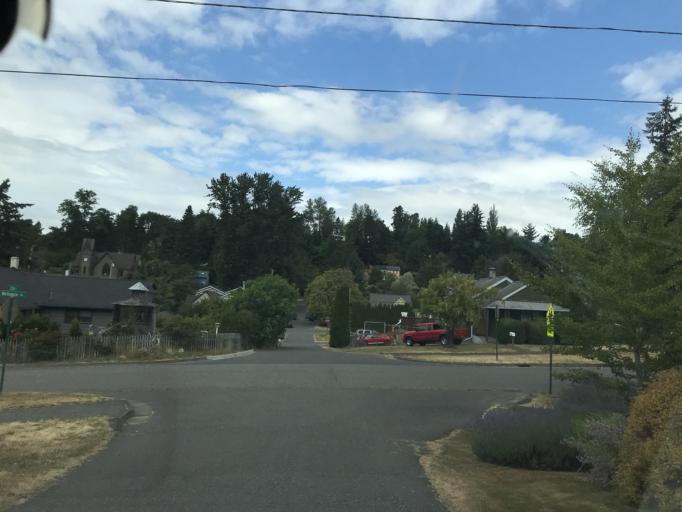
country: US
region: Washington
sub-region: Whatcom County
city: Bellingham
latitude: 48.7191
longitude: -122.4958
